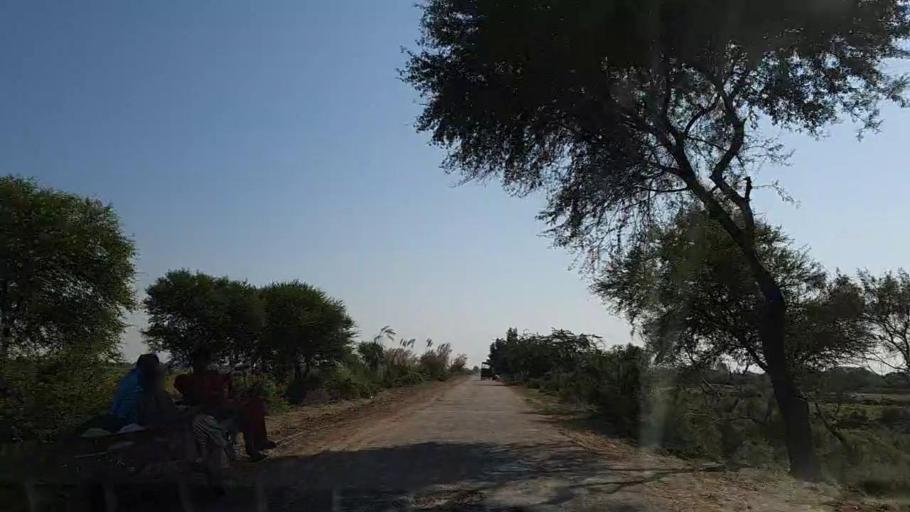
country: PK
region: Sindh
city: Chuhar Jamali
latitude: 24.5251
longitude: 68.0871
